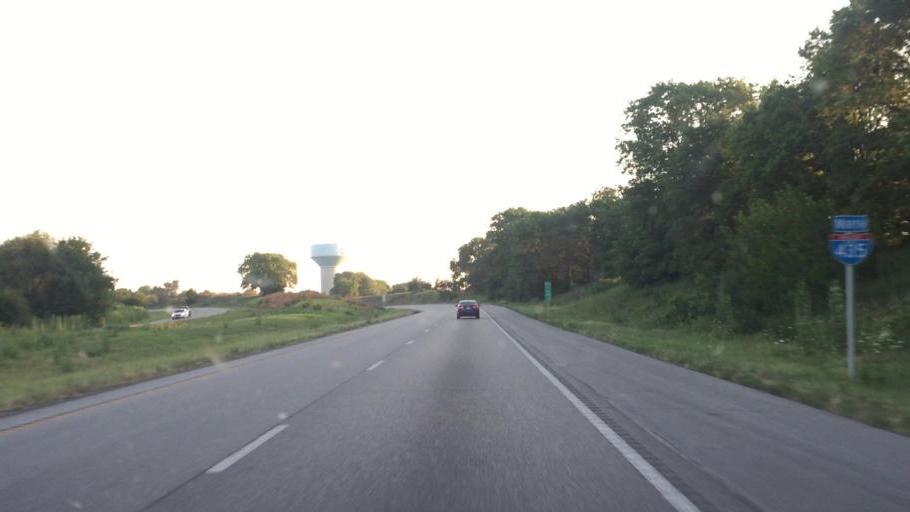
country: US
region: Missouri
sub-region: Clay County
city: Pleasant Valley
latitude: 39.3038
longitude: -94.5100
